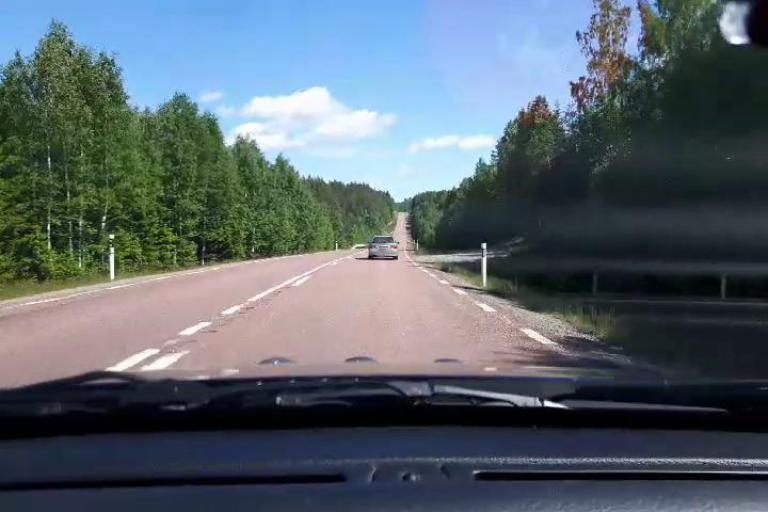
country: SE
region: Gaevleborg
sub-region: Hudiksvalls Kommun
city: Delsbo
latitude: 61.7644
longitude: 16.7644
